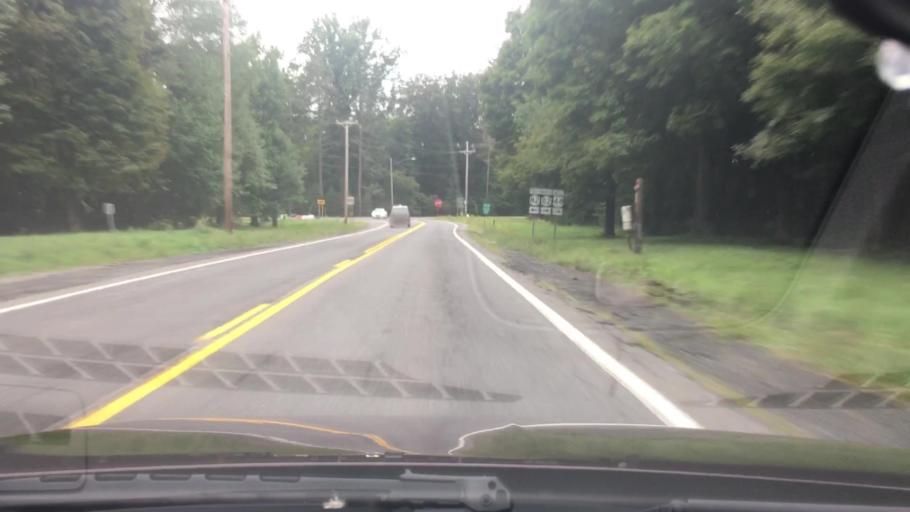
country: US
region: New York
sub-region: Dutchess County
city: Millbrook
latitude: 41.7809
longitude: -73.7356
